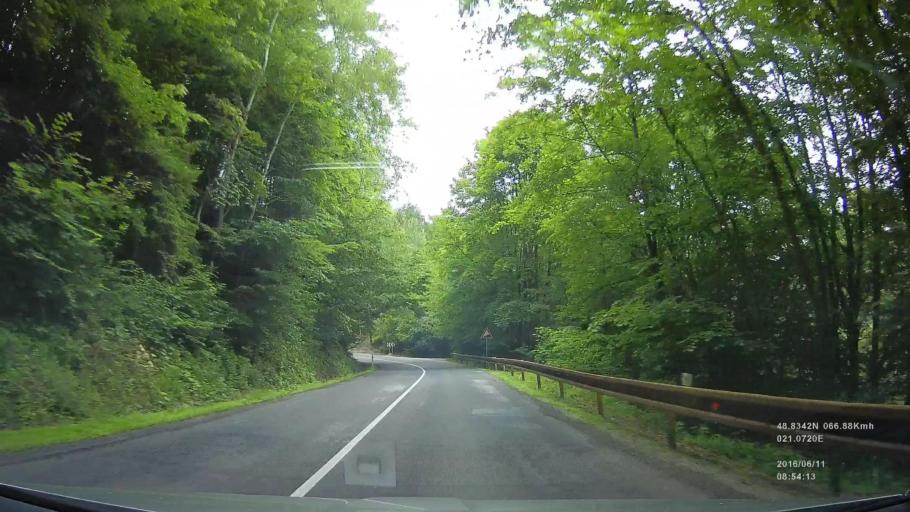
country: SK
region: Kosicky
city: Gelnica
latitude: 48.8313
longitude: 21.0774
